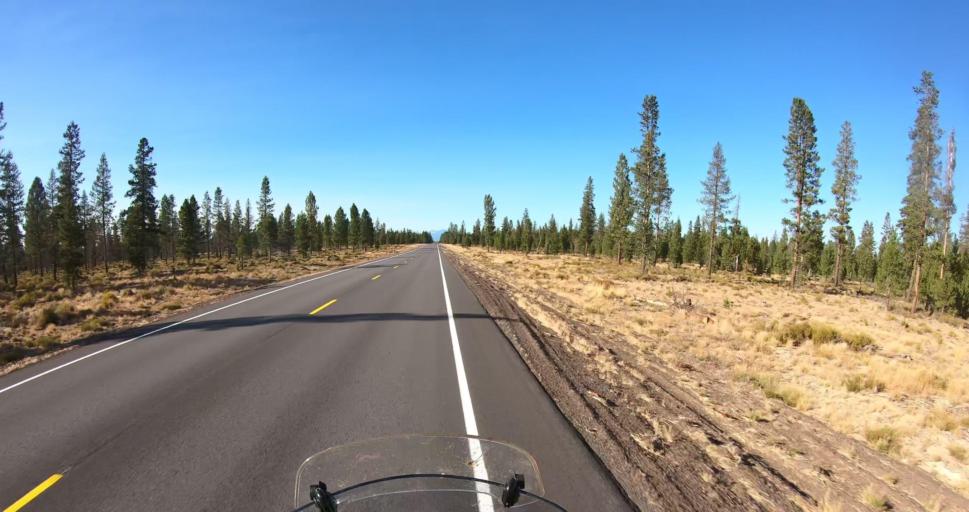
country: US
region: Oregon
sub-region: Deschutes County
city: La Pine
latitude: 43.5482
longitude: -121.4702
